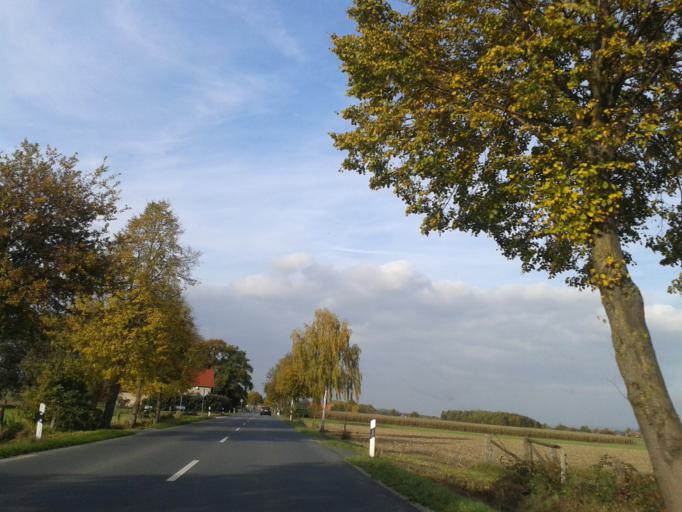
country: DE
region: North Rhine-Westphalia
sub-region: Regierungsbezirk Detmold
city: Salzkotten
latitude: 51.7277
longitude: 8.6633
